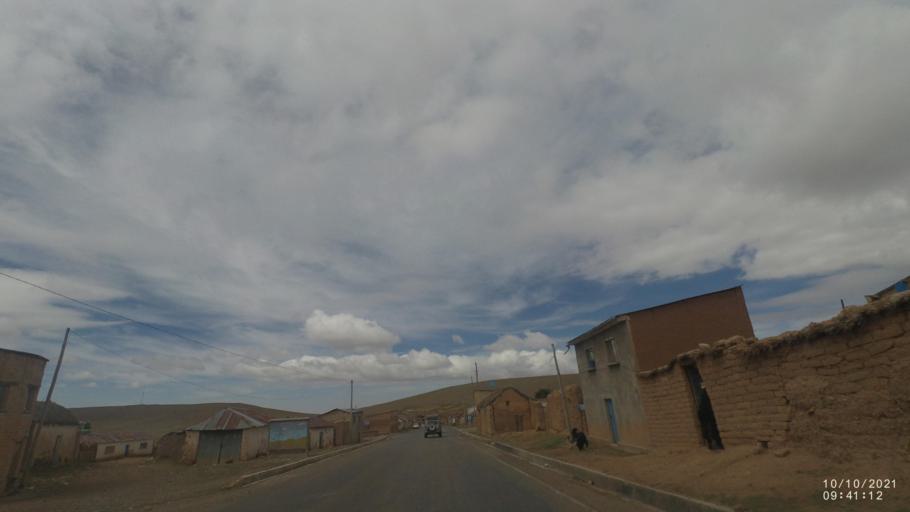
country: BO
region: La Paz
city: Quime
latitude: -17.1456
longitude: -67.3439
